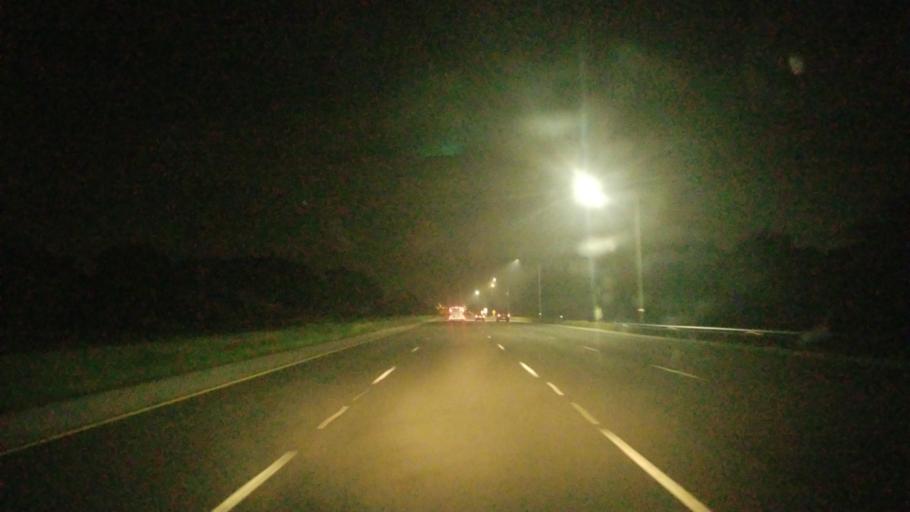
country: US
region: Illinois
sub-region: Madison County
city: Glen Carbon
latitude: 38.7568
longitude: -90.0137
